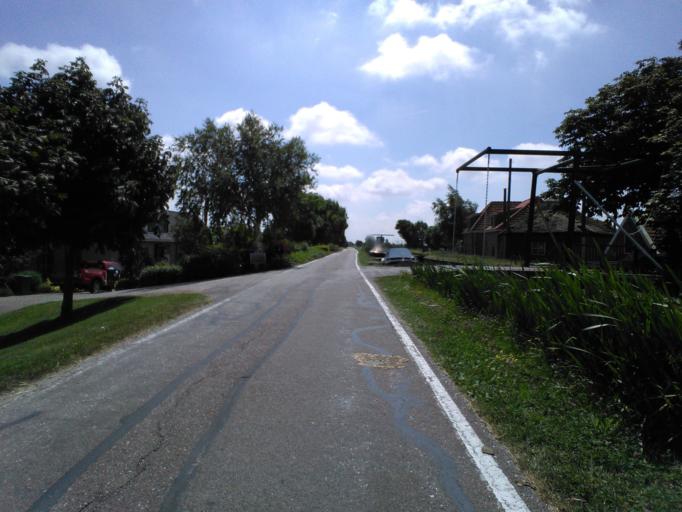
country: NL
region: South Holland
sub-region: Gemeente Maassluis
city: Maassluis
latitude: 51.9491
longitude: 4.2939
